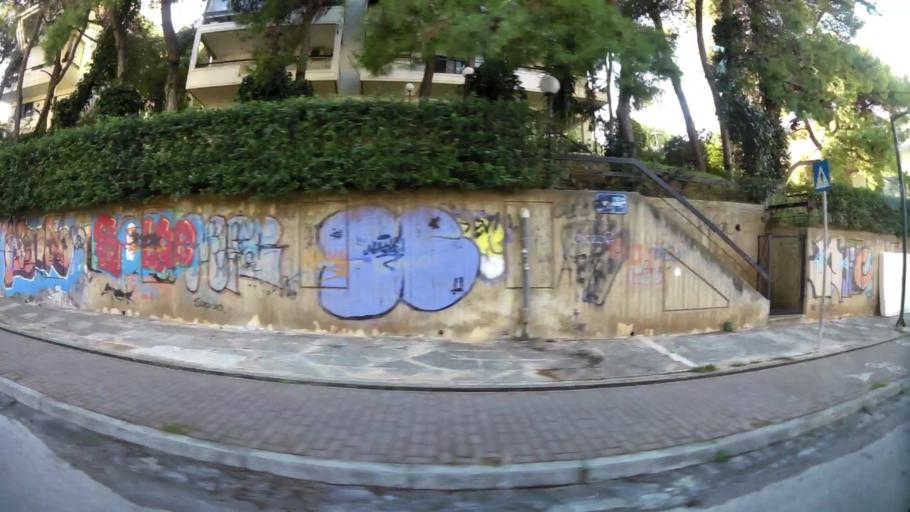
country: GR
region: Attica
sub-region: Nomarchia Athinas
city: Nea Erythraia
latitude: 38.0942
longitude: 23.8146
